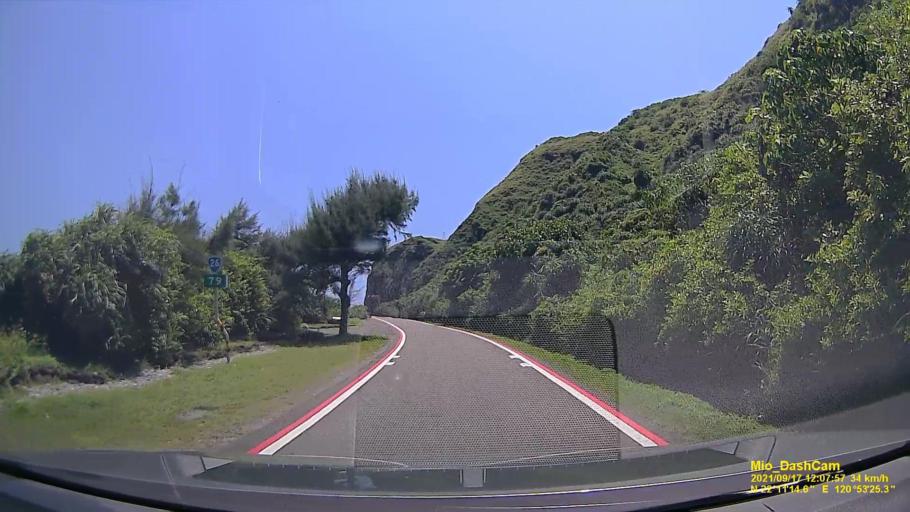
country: TW
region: Taiwan
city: Hengchun
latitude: 22.1875
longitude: 120.8903
